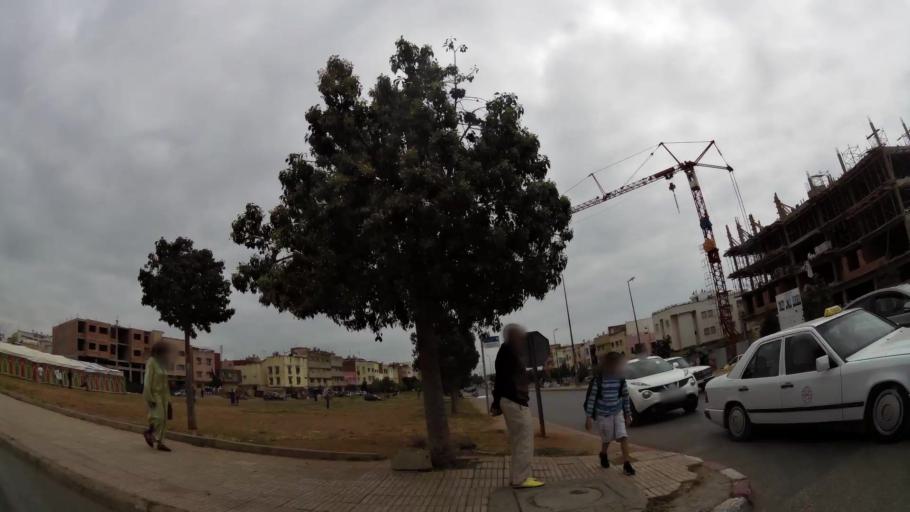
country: MA
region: Rabat-Sale-Zemmour-Zaer
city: Sale
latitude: 34.0320
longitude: -6.8035
